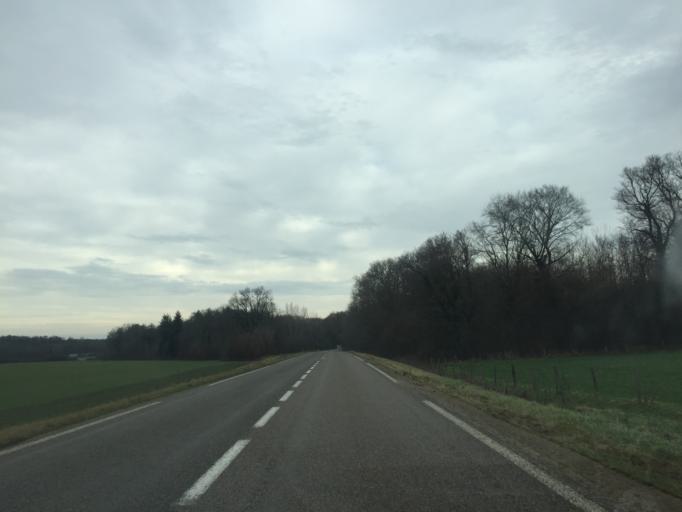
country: FR
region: Franche-Comte
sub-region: Departement du Jura
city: Poligny
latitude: 46.8425
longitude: 5.5728
